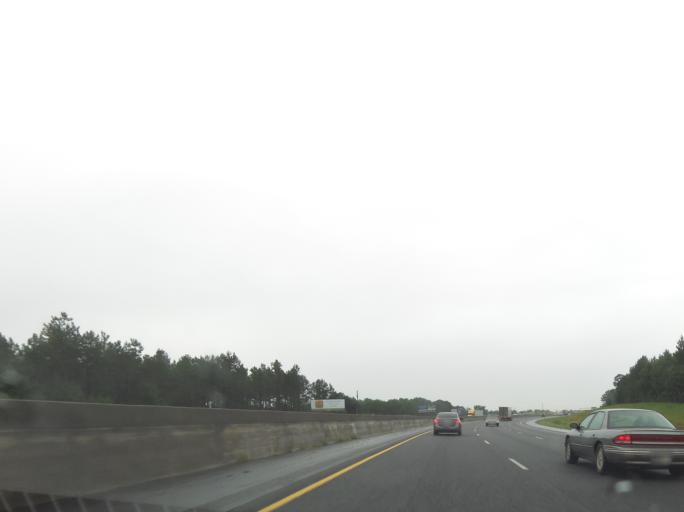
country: US
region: Georgia
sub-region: Tift County
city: Tifton
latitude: 31.5146
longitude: -83.5156
